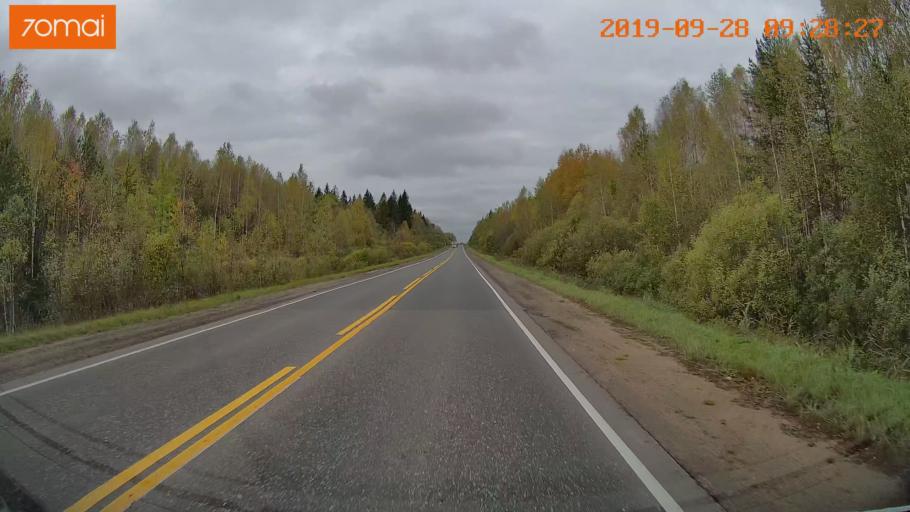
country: RU
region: Jaroslavl
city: Dubki
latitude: 57.2189
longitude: 40.2676
